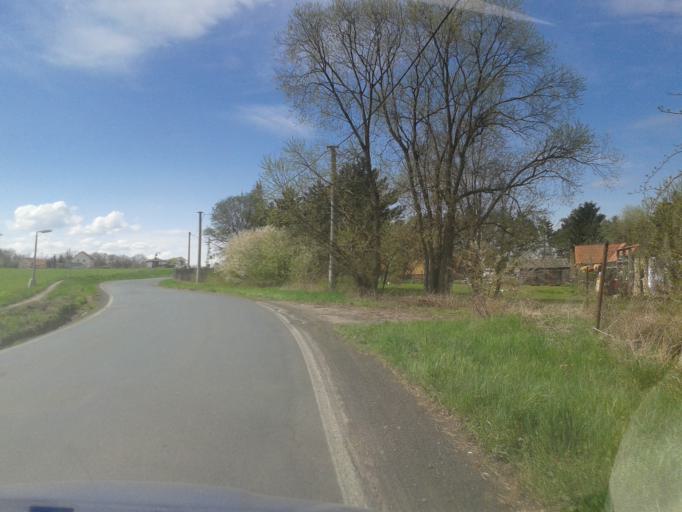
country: CZ
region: Central Bohemia
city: Dobris
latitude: 49.8754
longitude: 14.1459
